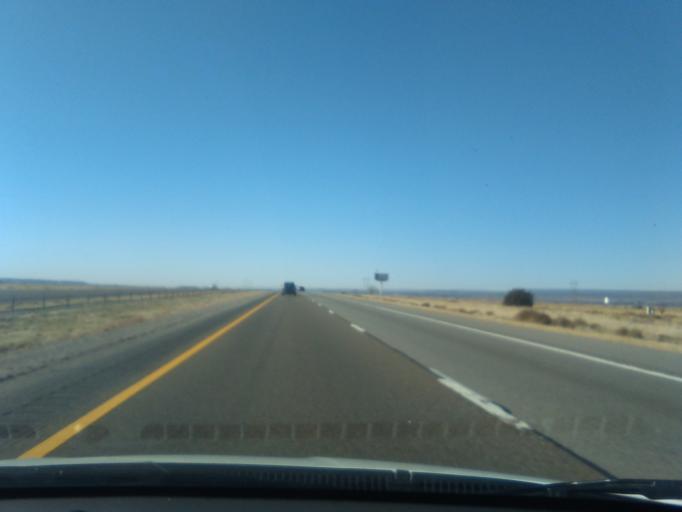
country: US
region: New Mexico
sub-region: Sandoval County
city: Santo Domingo Pueblo
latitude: 35.4510
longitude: -106.3518
